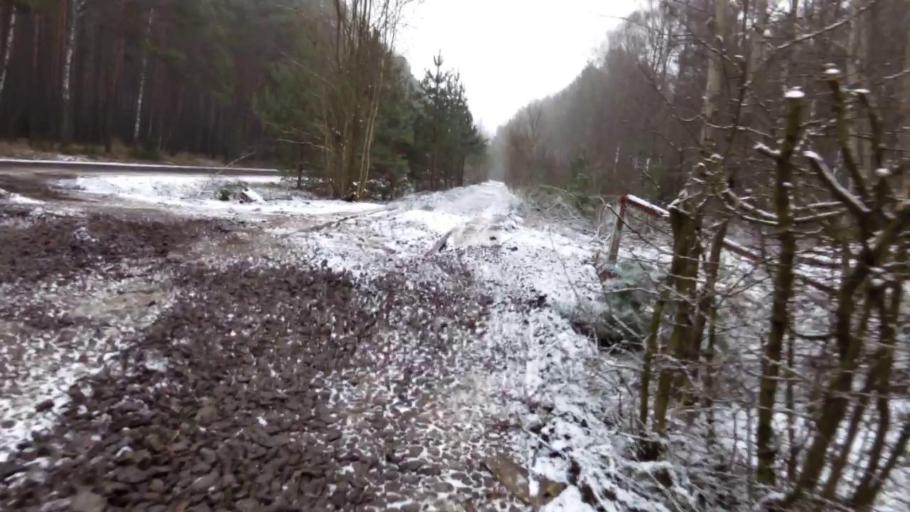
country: PL
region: West Pomeranian Voivodeship
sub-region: Powiat drawski
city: Wierzchowo
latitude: 53.4506
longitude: 16.1282
